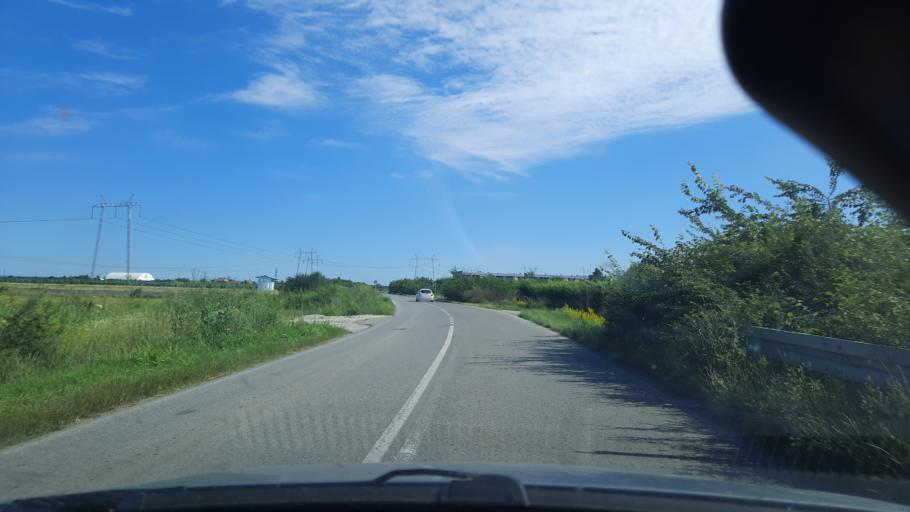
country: RS
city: Simanovci
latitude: 44.8530
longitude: 20.0996
